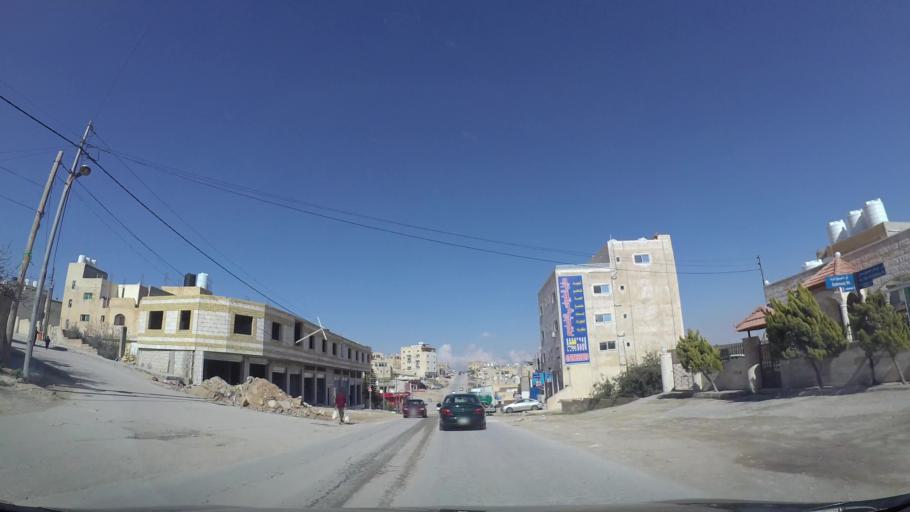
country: JO
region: Zarqa
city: Russeifa
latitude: 32.0385
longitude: 36.0507
